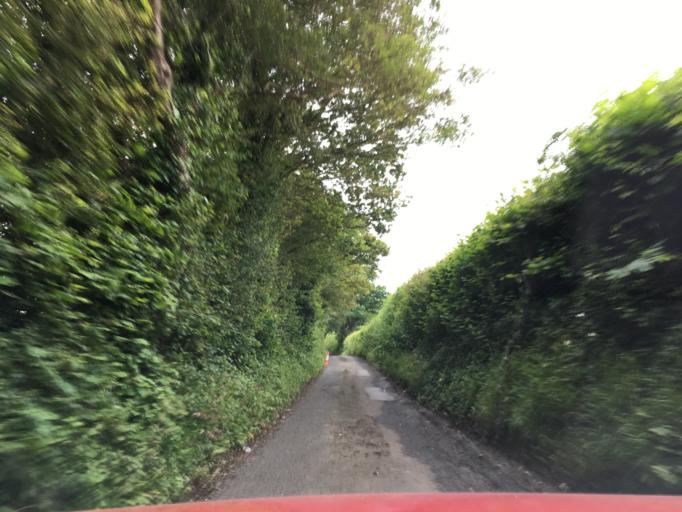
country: GB
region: England
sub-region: Bath and North East Somerset
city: Whitchurch
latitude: 51.4010
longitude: -2.5775
